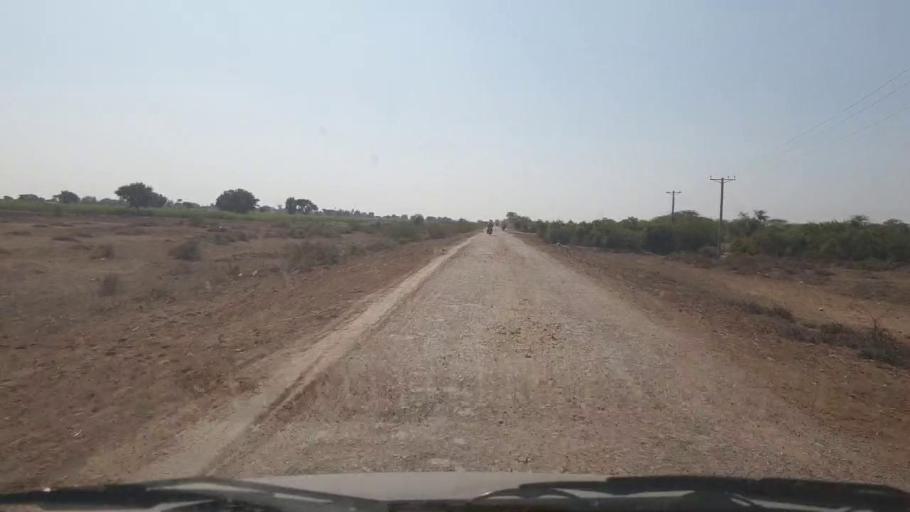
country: PK
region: Sindh
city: Samaro
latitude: 25.2274
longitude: 69.3348
